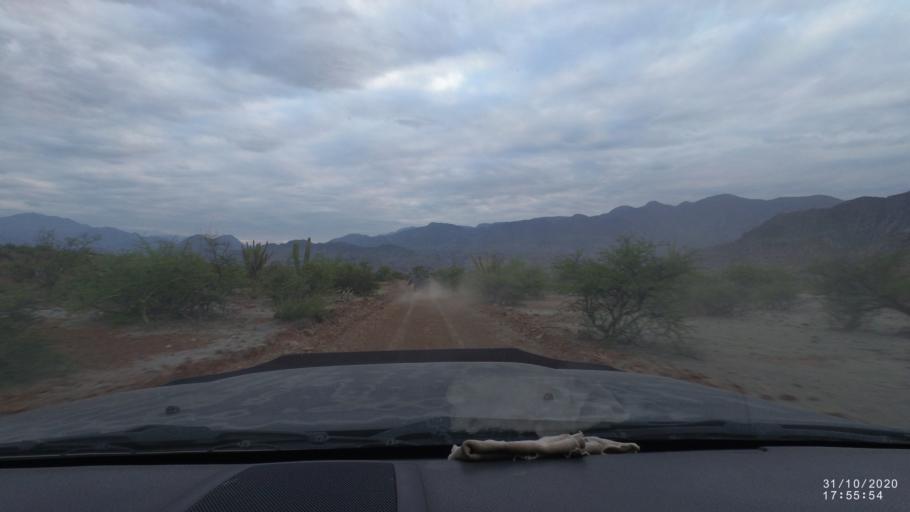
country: BO
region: Chuquisaca
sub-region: Provincia Zudanez
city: Mojocoya
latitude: -18.6474
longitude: -64.5287
